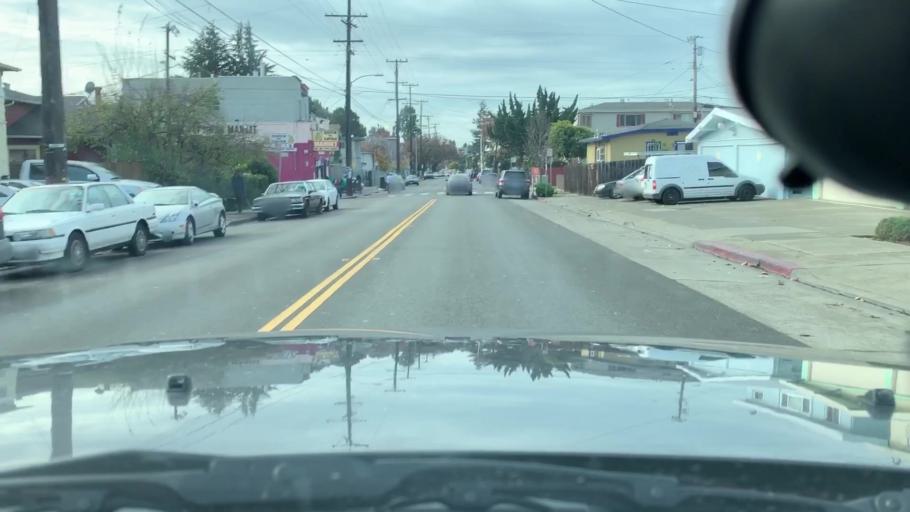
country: US
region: California
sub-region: Alameda County
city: Alameda
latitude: 37.7863
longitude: -122.2135
